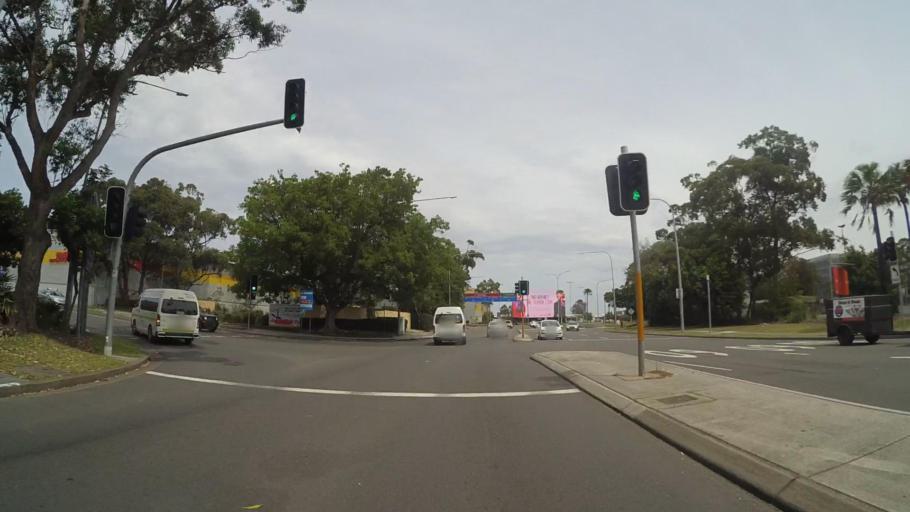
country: AU
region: New South Wales
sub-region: Botany Bay
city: Mascot
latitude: -33.9328
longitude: 151.1860
